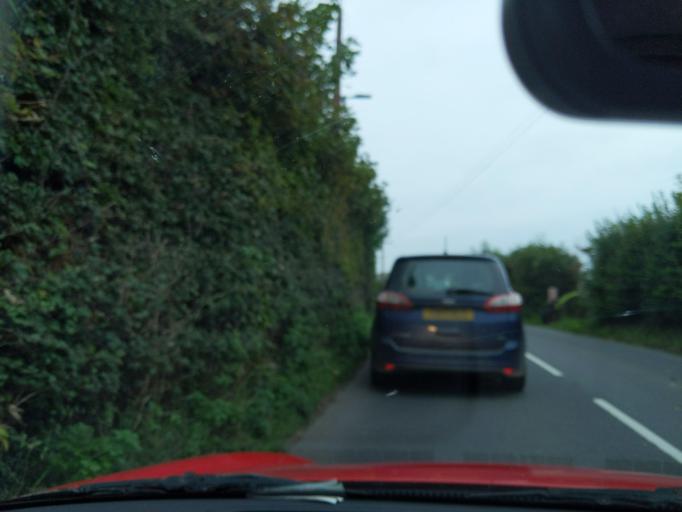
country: GB
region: England
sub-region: Devon
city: Winkleigh
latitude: 50.8558
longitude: -4.0639
